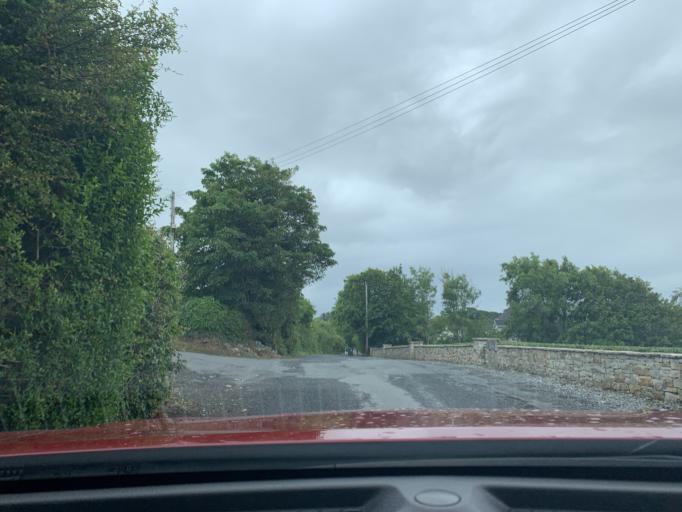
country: IE
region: Connaught
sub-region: Sligo
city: Sligo
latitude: 54.3124
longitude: -8.4770
